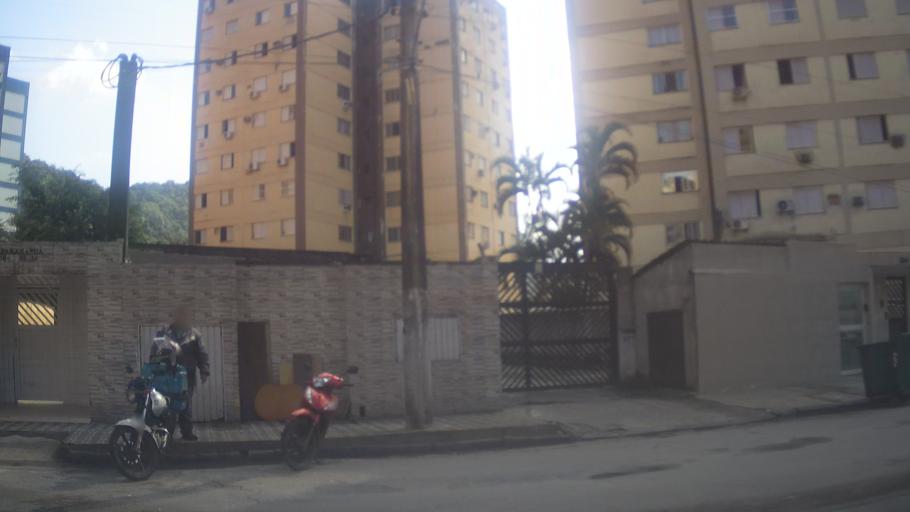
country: BR
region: Sao Paulo
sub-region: Santos
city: Santos
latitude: -23.9339
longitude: -46.3480
